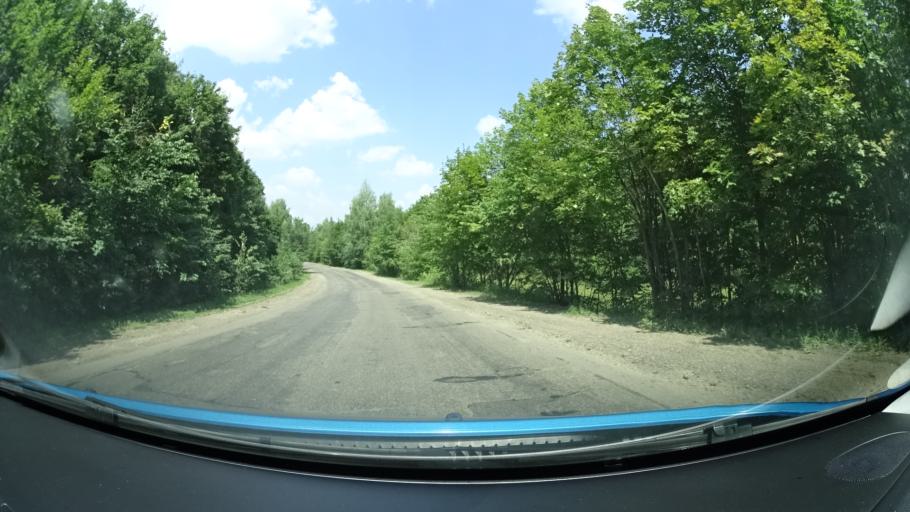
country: RU
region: Bashkortostan
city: Oktyabr'skiy
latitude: 54.4740
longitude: 53.5783
